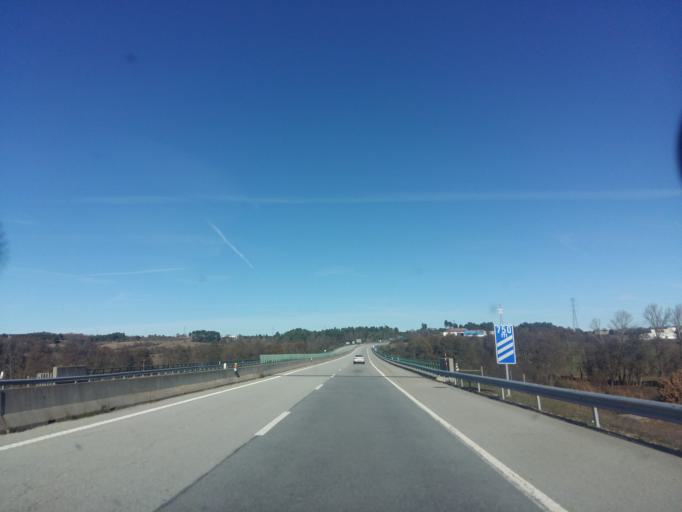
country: PT
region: Guarda
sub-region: Guarda
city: Guarda
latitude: 40.5141
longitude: -7.2333
